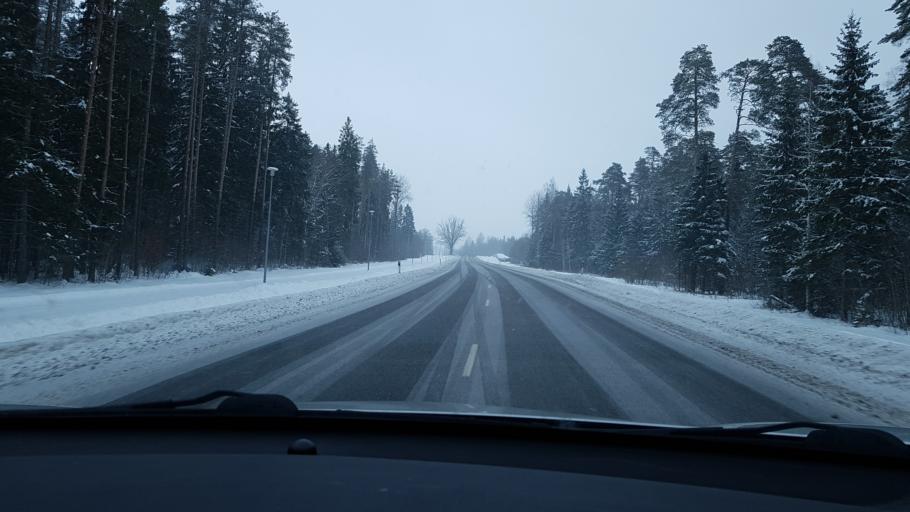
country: EE
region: Jaervamaa
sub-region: Paide linn
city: Paide
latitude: 58.8630
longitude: 25.4911
